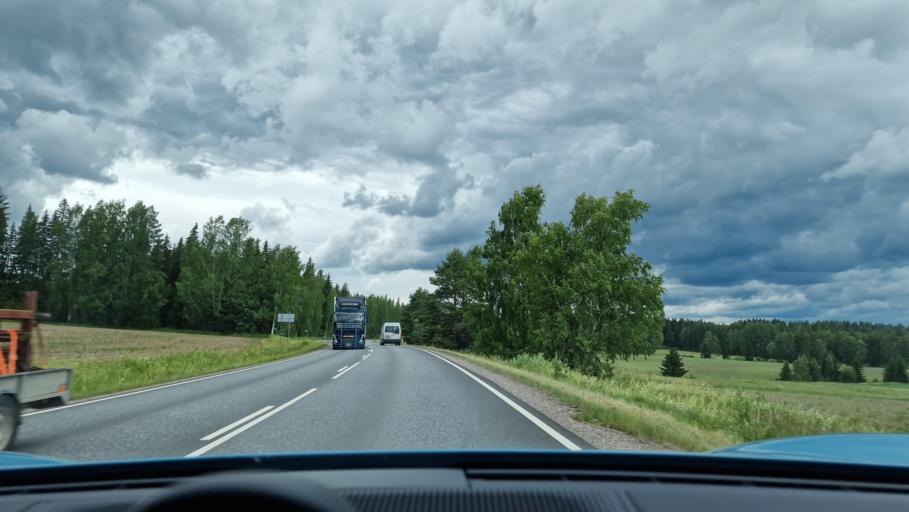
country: FI
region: Pirkanmaa
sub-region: Ylae-Pirkanmaa
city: Ruovesi
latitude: 62.0355
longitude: 24.0107
